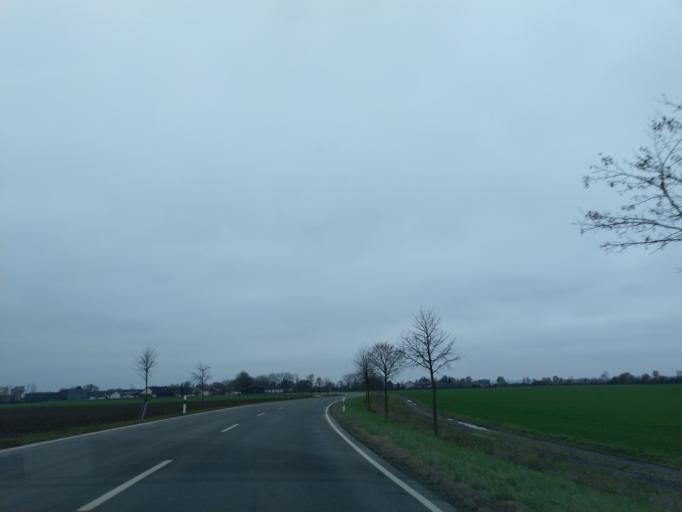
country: DE
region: Bavaria
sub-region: Lower Bavaria
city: Otzing
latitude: 48.7727
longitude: 12.7916
